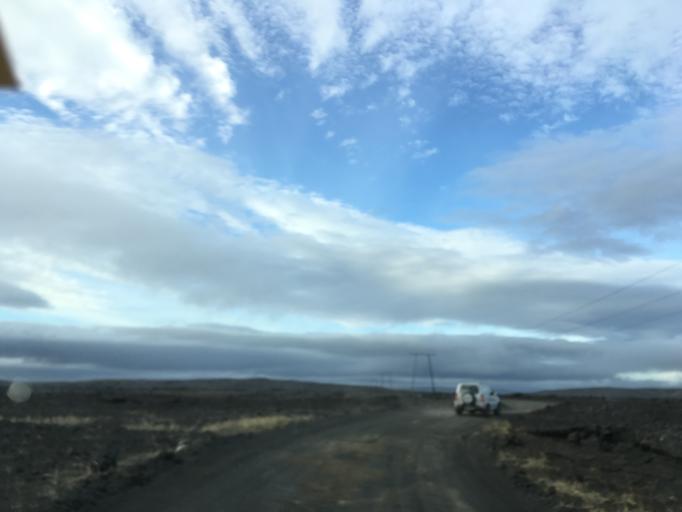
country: IS
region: South
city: Vestmannaeyjar
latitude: 64.1362
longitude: -19.1268
